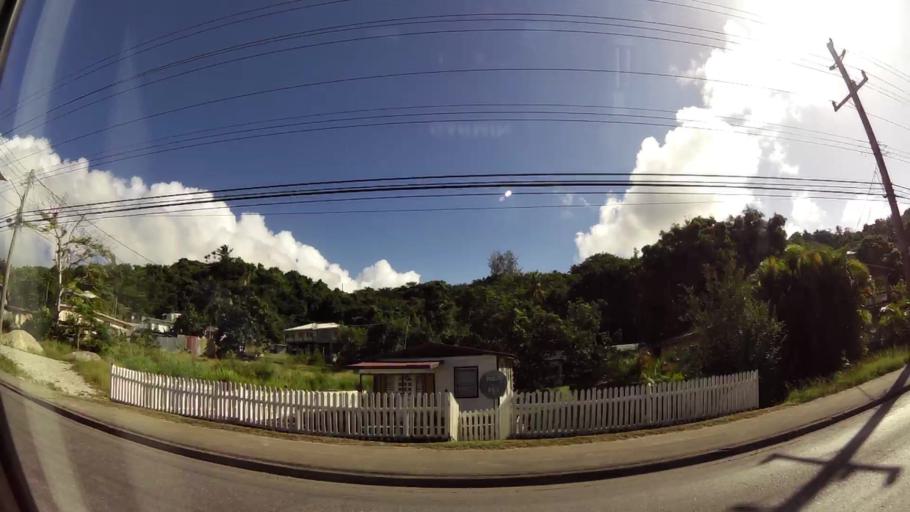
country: BB
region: Saint James
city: Holetown
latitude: 13.2154
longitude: -59.6195
